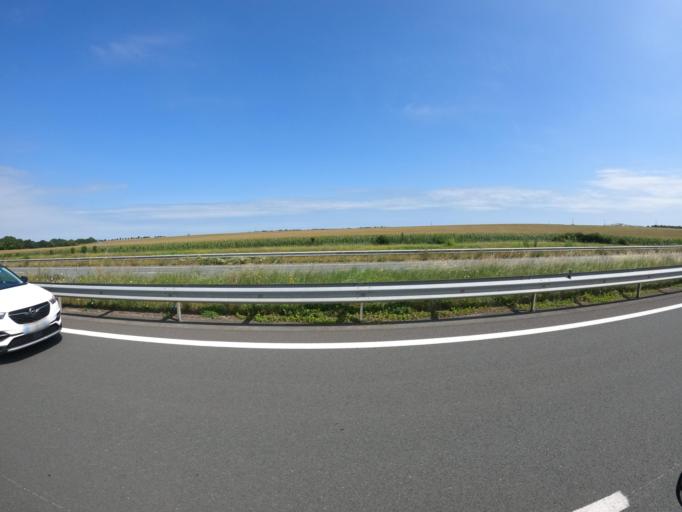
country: FR
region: Poitou-Charentes
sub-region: Departement des Deux-Sevres
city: Mauze-sur-le-Mignon
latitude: 46.2013
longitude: -0.7130
